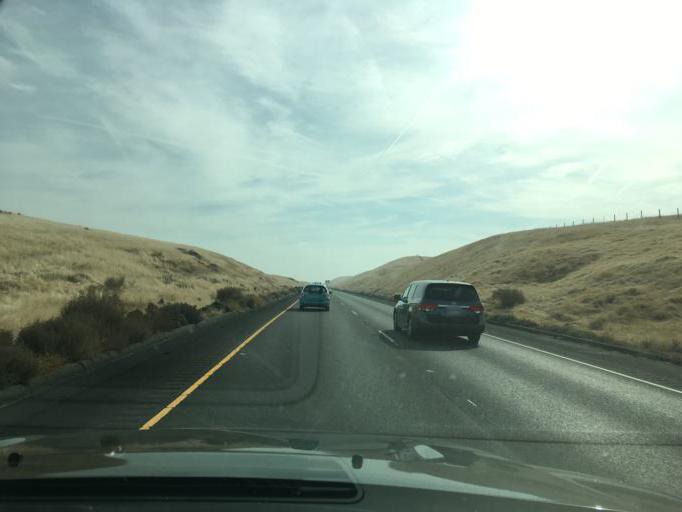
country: US
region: California
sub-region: Kings County
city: Kettleman City
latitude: 36.0045
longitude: -119.9838
